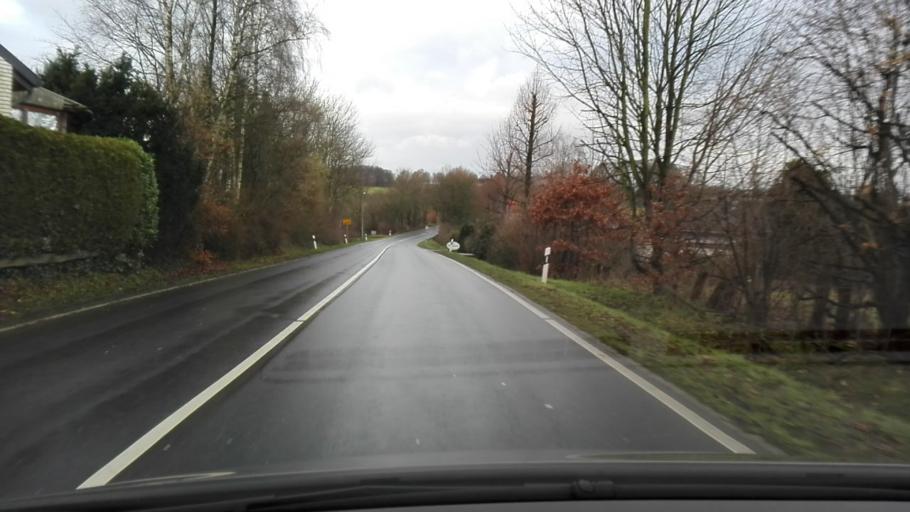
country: DE
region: North Rhine-Westphalia
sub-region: Regierungsbezirk Arnsberg
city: Frondenberg
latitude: 51.4930
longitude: 7.7765
